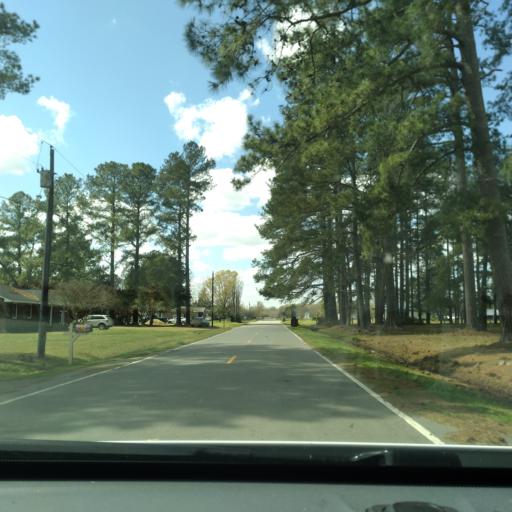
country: US
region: North Carolina
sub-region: Washington County
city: Plymouth
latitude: 35.8335
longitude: -76.7157
